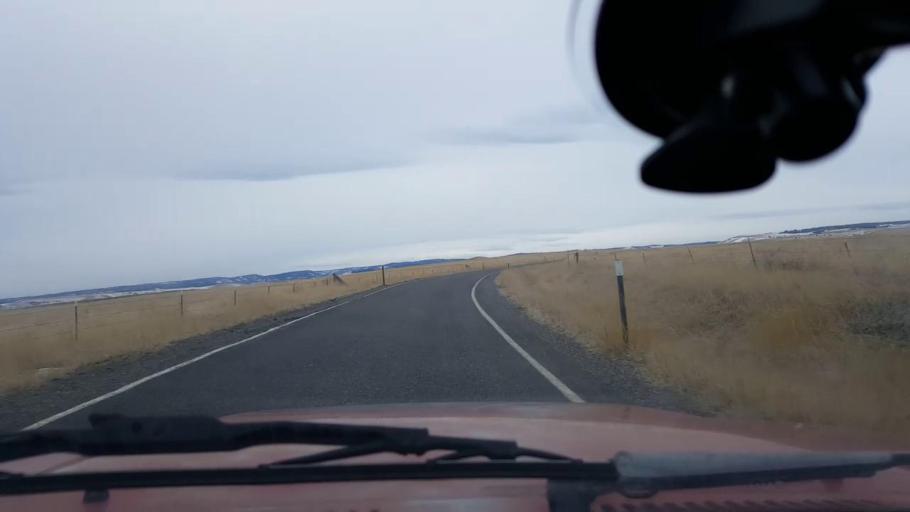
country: US
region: Washington
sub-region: Asotin County
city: Clarkston Heights-Vineland
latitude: 46.3149
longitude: -117.3303
